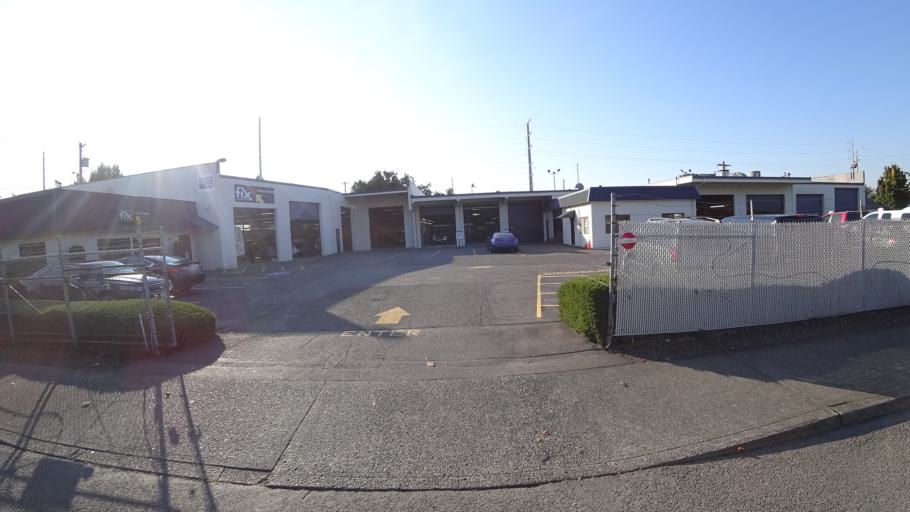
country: US
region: Oregon
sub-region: Multnomah County
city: Gresham
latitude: 45.5156
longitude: -122.4552
